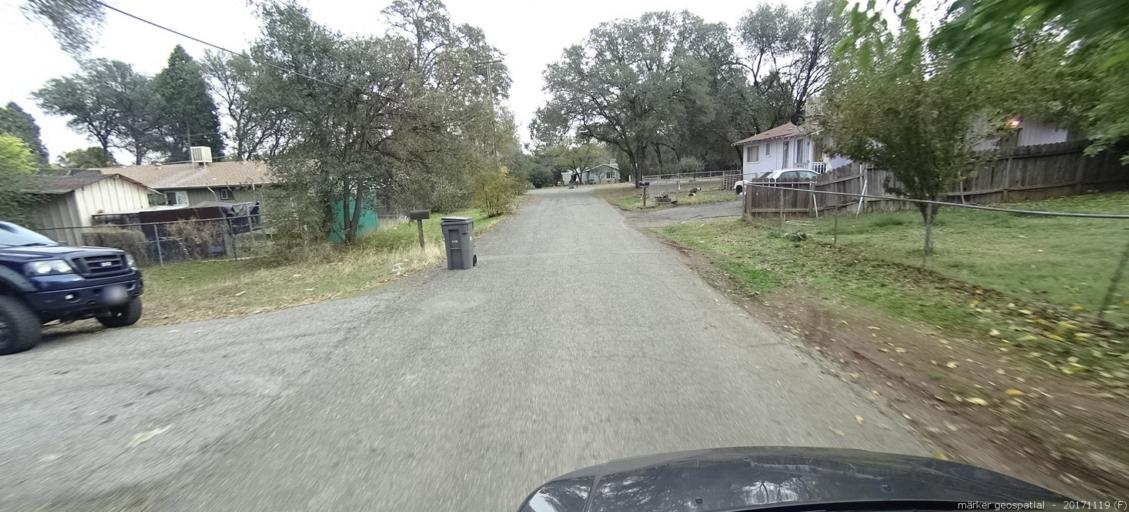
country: US
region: California
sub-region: Shasta County
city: Anderson
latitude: 40.4883
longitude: -122.3688
